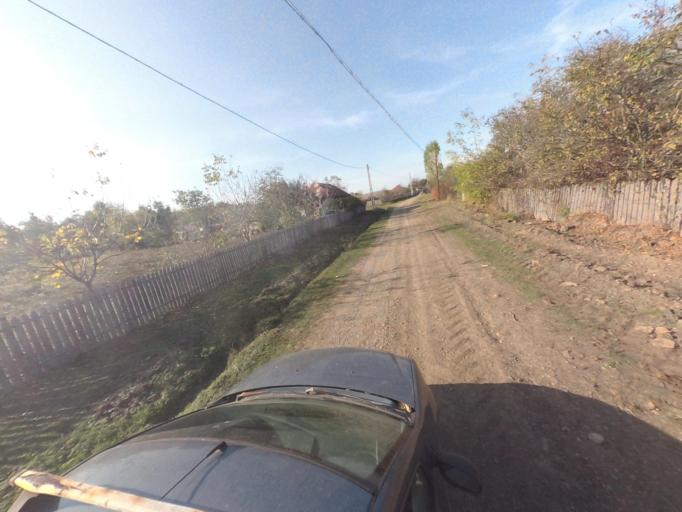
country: RO
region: Vaslui
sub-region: Comuna Bacesti
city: Bacesti
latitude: 46.8733
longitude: 27.1970
